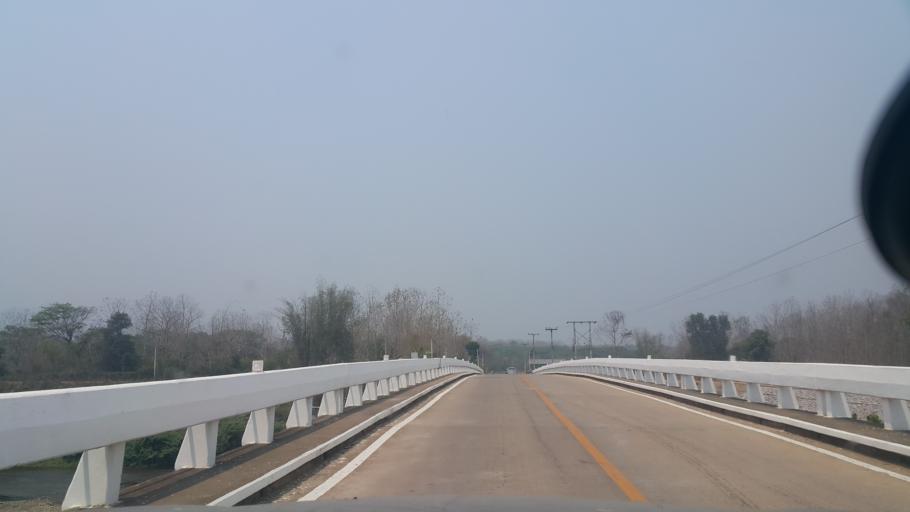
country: TH
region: Lampang
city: Sop Prap
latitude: 17.8901
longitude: 99.3283
